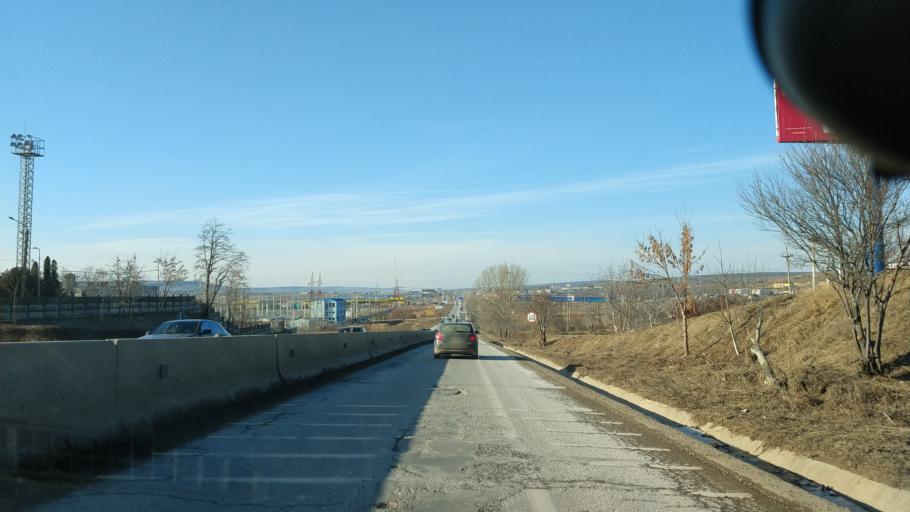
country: RO
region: Iasi
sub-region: Comuna Valea Lupului
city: Valea Lupului
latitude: 47.1780
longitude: 27.4864
